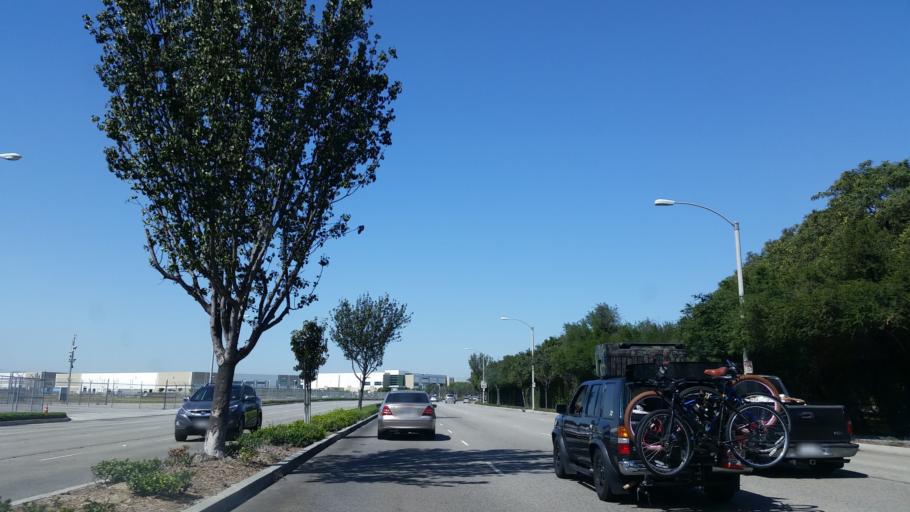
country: US
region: California
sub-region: Los Angeles County
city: Lakewood
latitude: 33.8224
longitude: -118.1409
